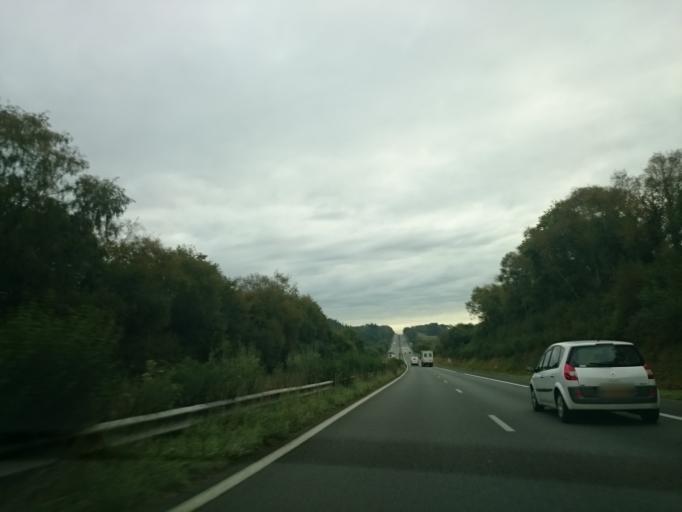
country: FR
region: Brittany
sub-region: Departement du Finistere
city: Pont-Aven
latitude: 47.8845
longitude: -3.7418
